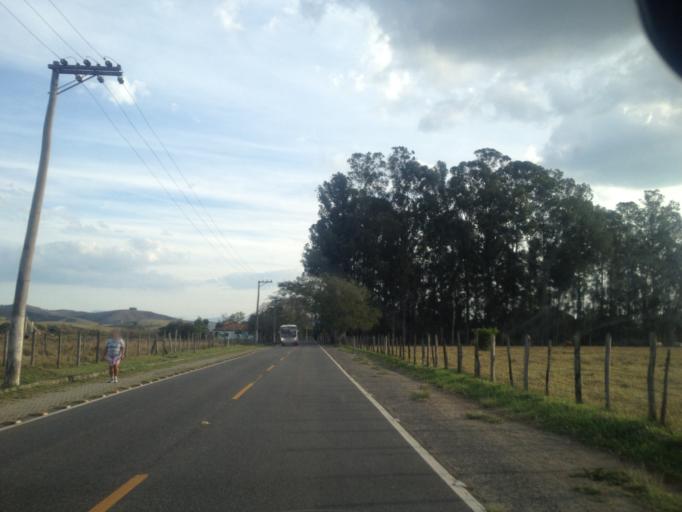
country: BR
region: Rio de Janeiro
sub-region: Quatis
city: Quatis
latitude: -22.4076
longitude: -44.2703
